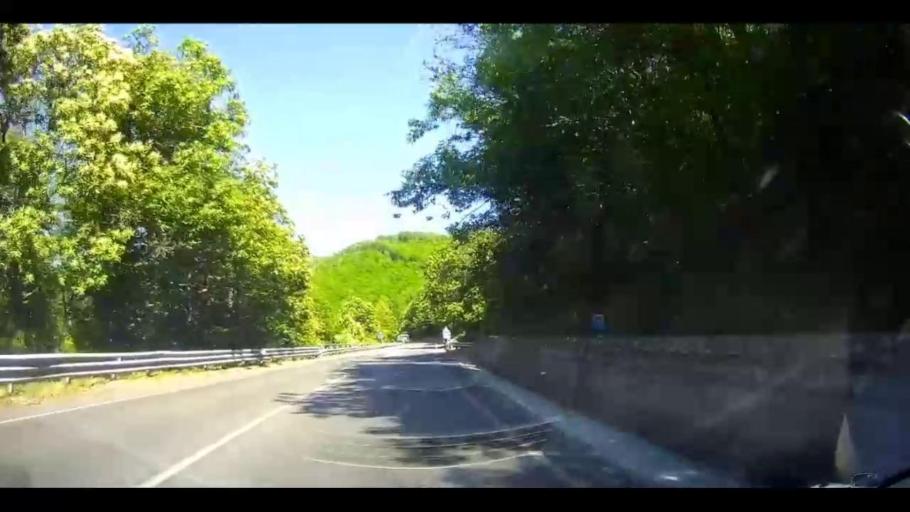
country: IT
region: Calabria
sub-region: Provincia di Cosenza
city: Celico
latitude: 39.3150
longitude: 16.3562
